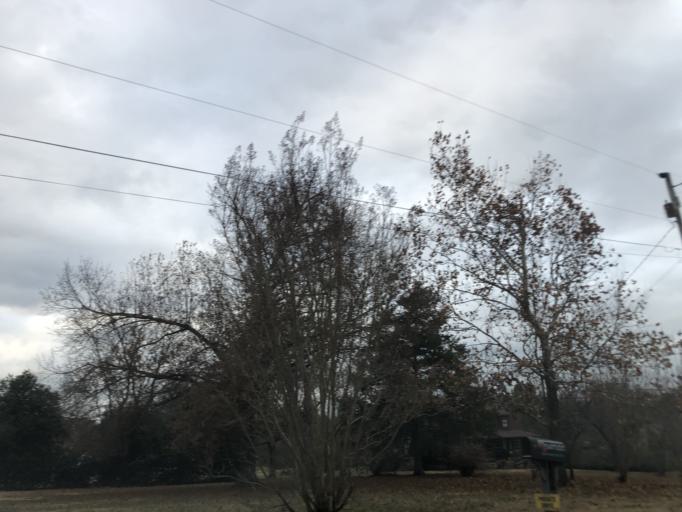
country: US
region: Tennessee
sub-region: Davidson County
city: Goodlettsville
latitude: 36.2991
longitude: -86.6822
